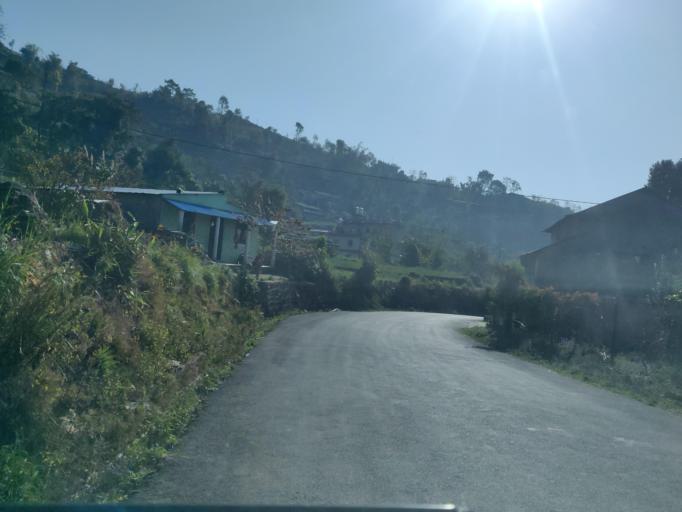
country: NP
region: Western Region
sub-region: Gandaki Zone
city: Pokhara
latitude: 28.2373
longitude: 83.9638
